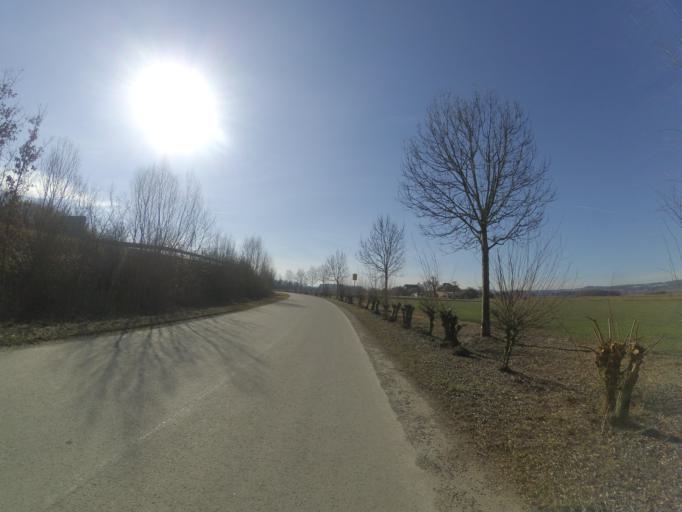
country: DE
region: Baden-Wuerttemberg
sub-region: Tuebingen Region
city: Baindt
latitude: 47.8503
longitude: 9.6379
